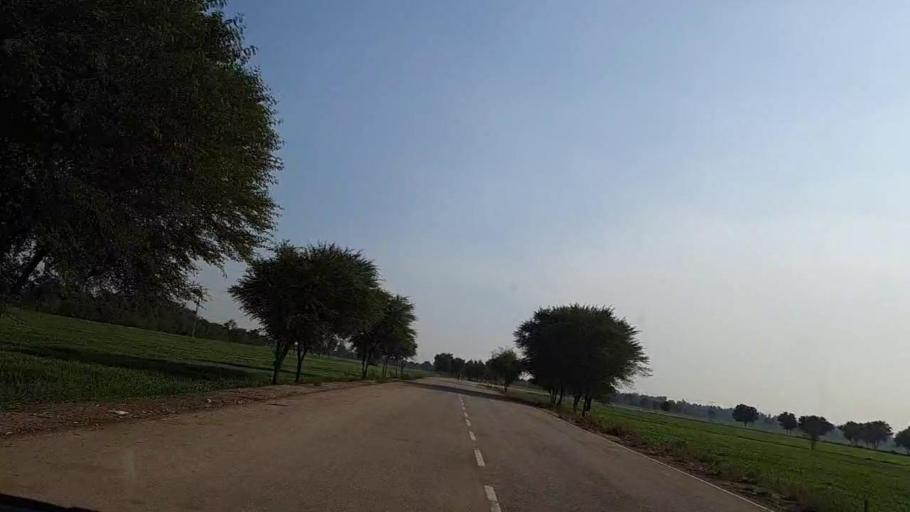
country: PK
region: Sindh
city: Sakrand
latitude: 26.1197
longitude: 68.2492
